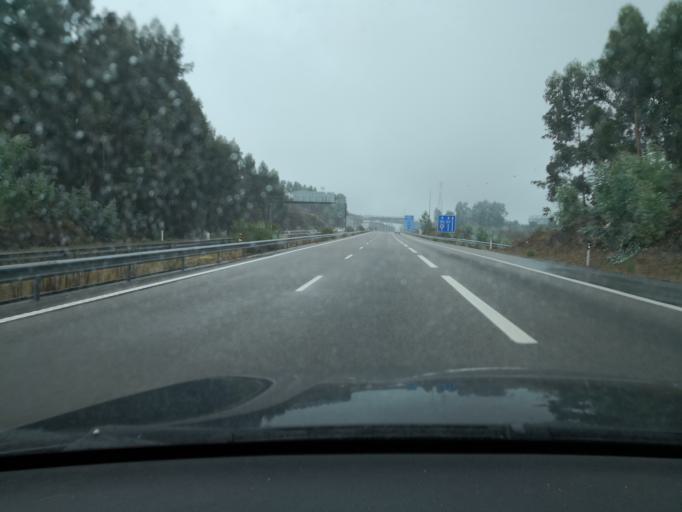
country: PT
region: Porto
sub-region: Pacos de Ferreira
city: Seroa
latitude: 41.2415
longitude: -8.4354
